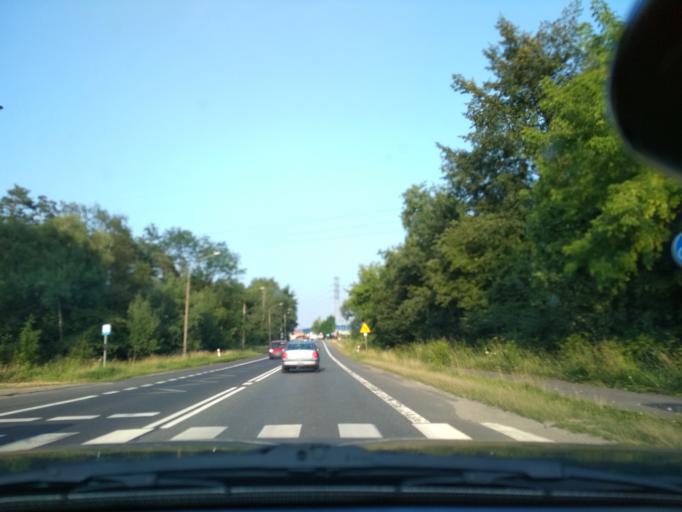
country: PL
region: Silesian Voivodeship
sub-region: Powiat zawiercianski
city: Zawiercie
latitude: 50.4771
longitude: 19.4605
